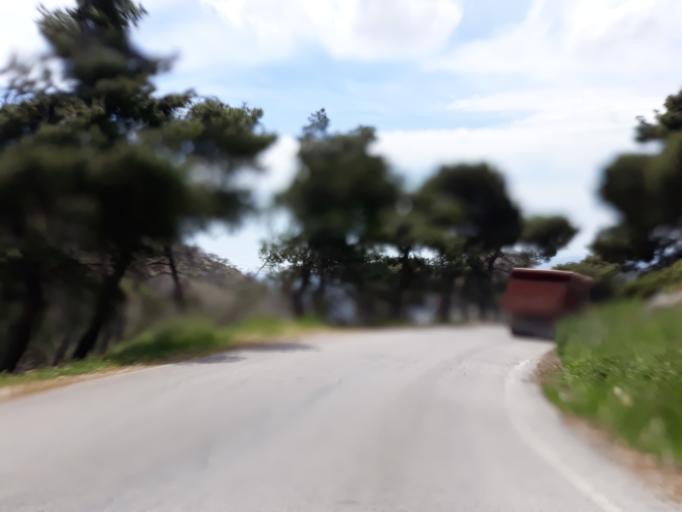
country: GR
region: Attica
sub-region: Nomarchia Dytikis Attikis
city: Magoula
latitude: 38.1561
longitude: 23.5308
